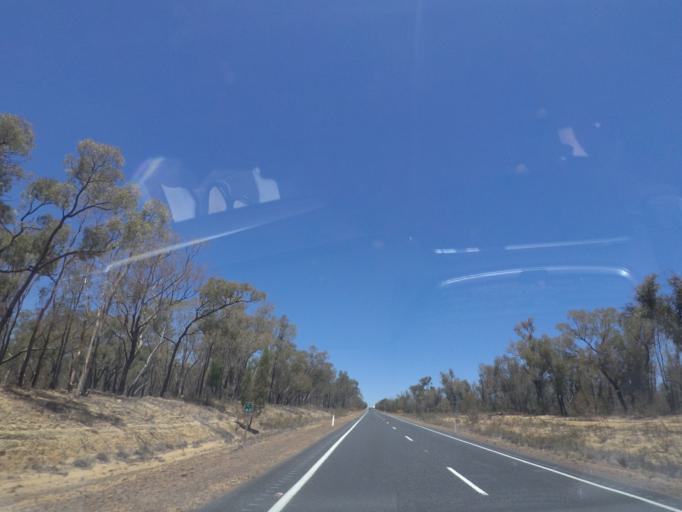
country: AU
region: New South Wales
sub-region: Warrumbungle Shire
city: Coonabarabran
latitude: -30.9534
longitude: 149.4209
